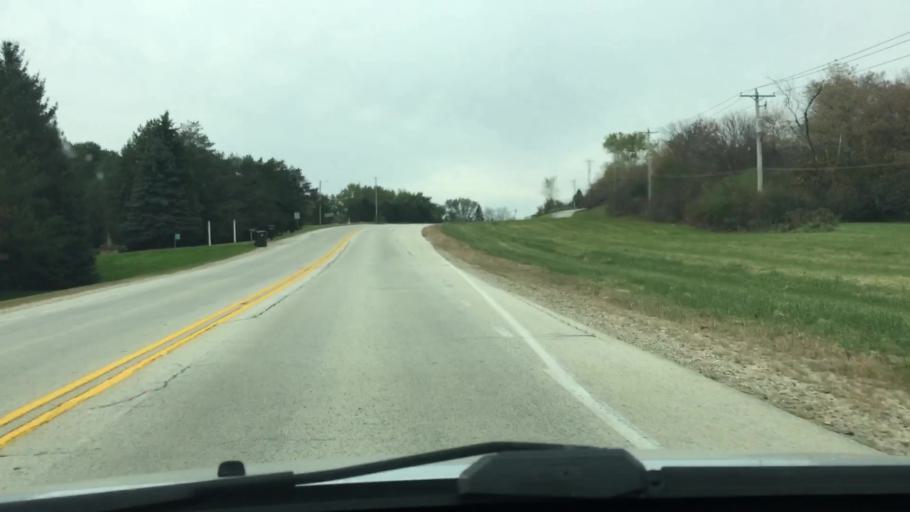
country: US
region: Wisconsin
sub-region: Waukesha County
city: Big Bend
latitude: 42.9050
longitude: -88.2462
